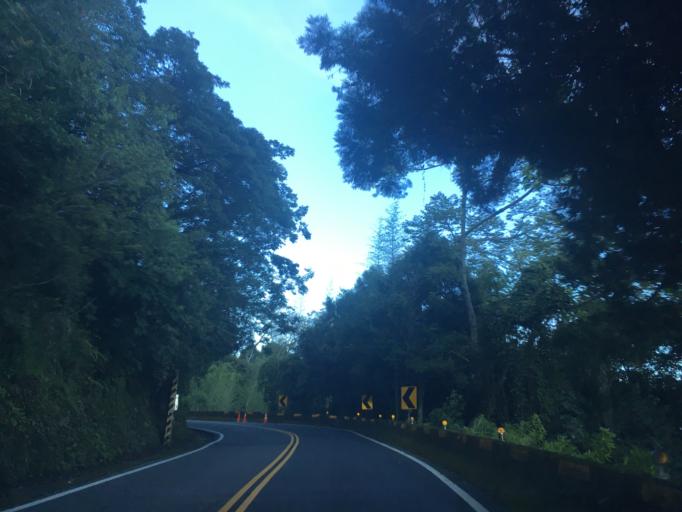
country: TW
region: Taiwan
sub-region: Nantou
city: Puli
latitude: 24.0361
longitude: 121.1484
